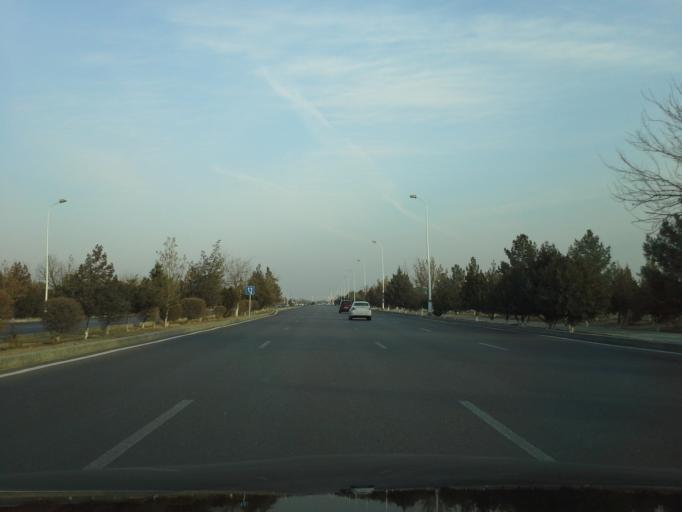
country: TM
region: Ahal
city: Abadan
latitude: 38.0372
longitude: 58.2174
